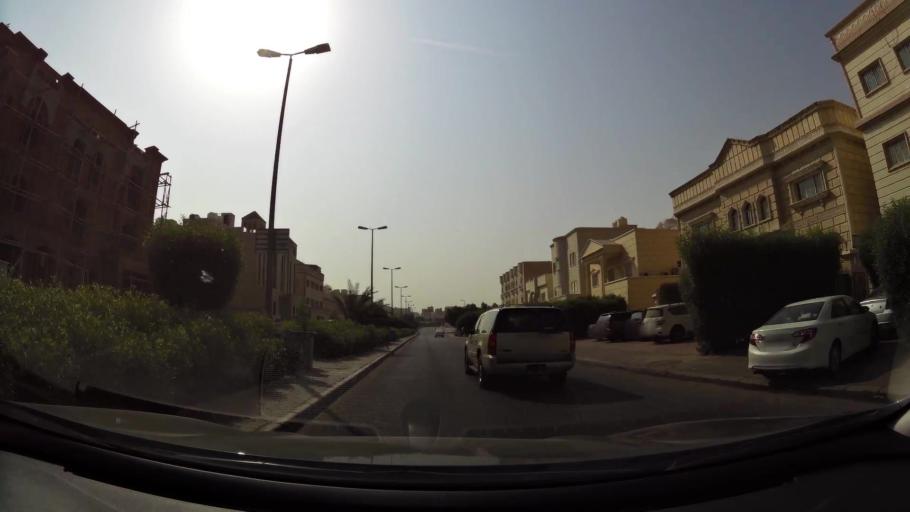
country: KW
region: Al Asimah
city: Ar Rabiyah
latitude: 29.2748
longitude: 47.8942
